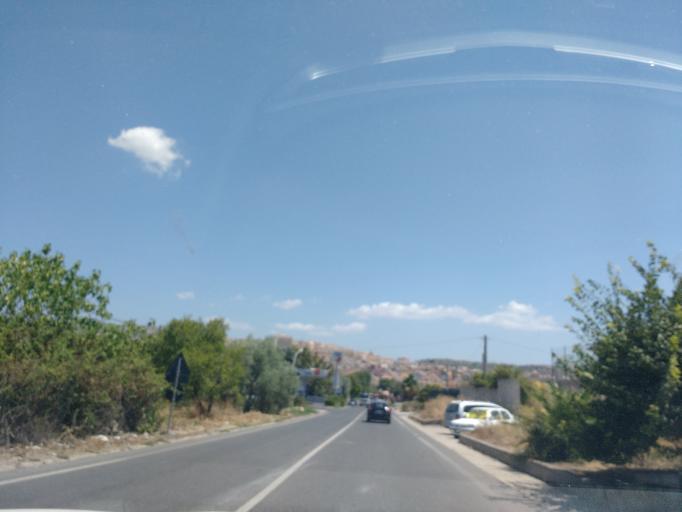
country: IT
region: Sicily
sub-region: Provincia di Siracusa
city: Noto
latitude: 36.8807
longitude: 15.0609
